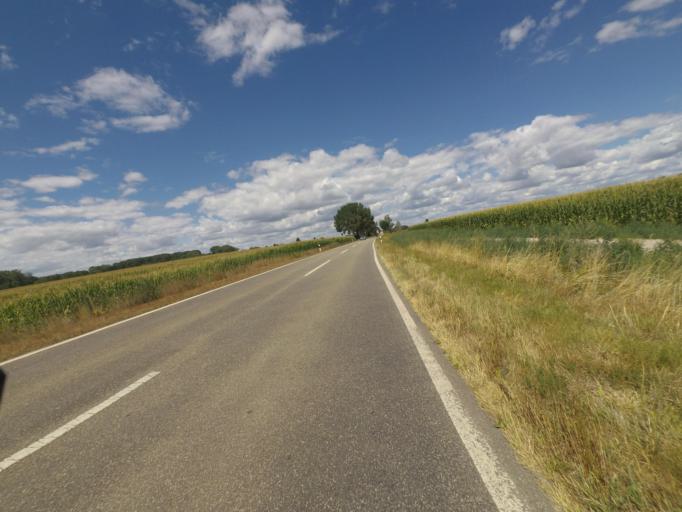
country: DE
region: Baden-Wuerttemberg
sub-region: Karlsruhe Region
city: Ottenhofen
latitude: 48.7465
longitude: 8.1026
